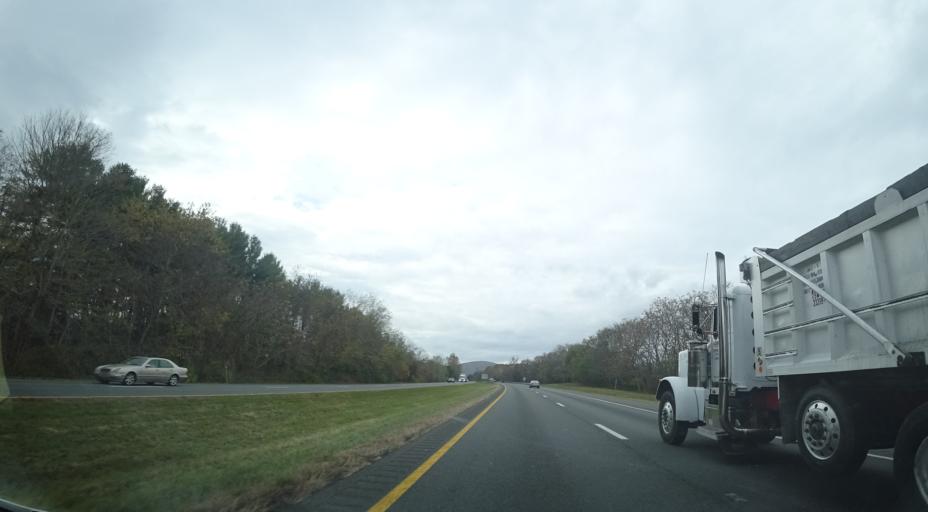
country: US
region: Virginia
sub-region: Fauquier County
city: Marshall
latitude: 38.9000
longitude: -77.9216
